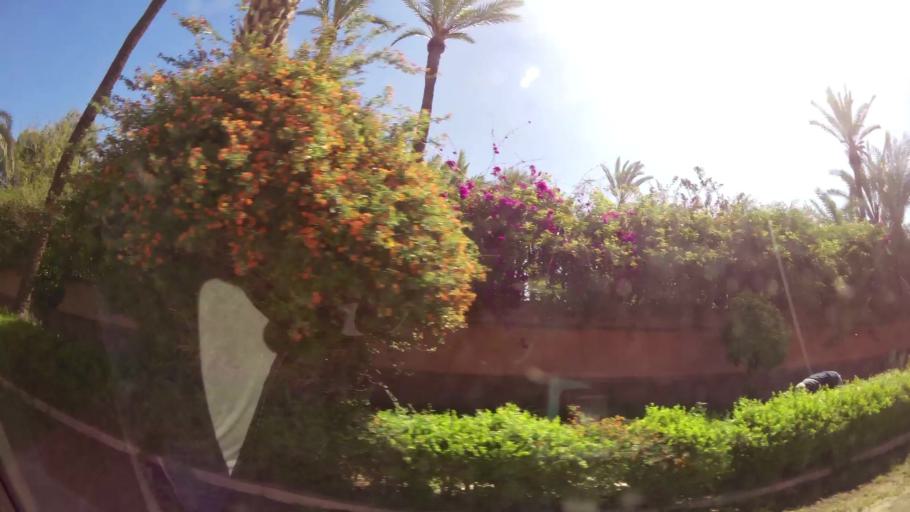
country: MA
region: Marrakech-Tensift-Al Haouz
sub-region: Marrakech
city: Marrakesh
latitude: 31.6546
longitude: -7.9655
